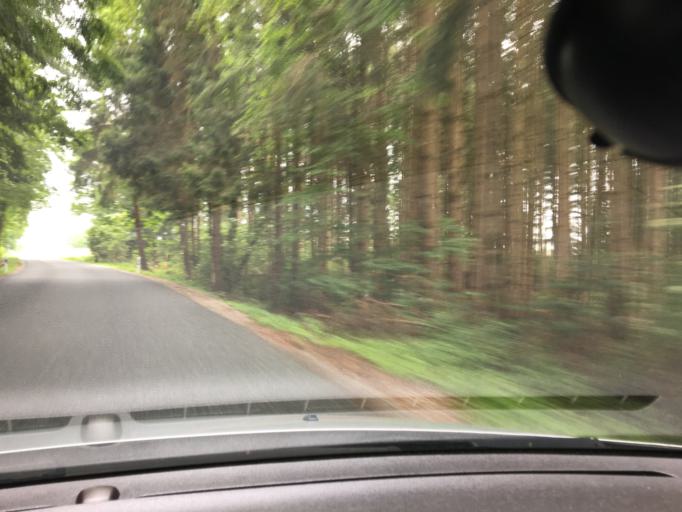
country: DE
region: Bavaria
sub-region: Upper Bavaria
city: Otterfing
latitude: 47.9258
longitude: 11.6536
